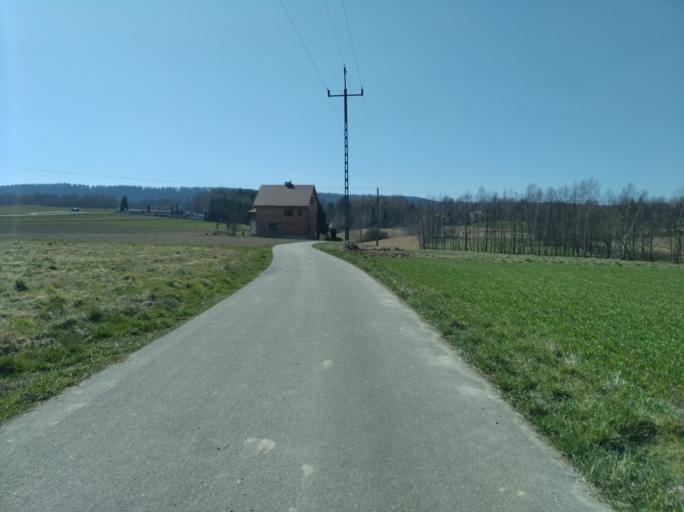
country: PL
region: Subcarpathian Voivodeship
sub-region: Powiat strzyzowski
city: Strzyzow
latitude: 49.8408
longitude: 21.8156
